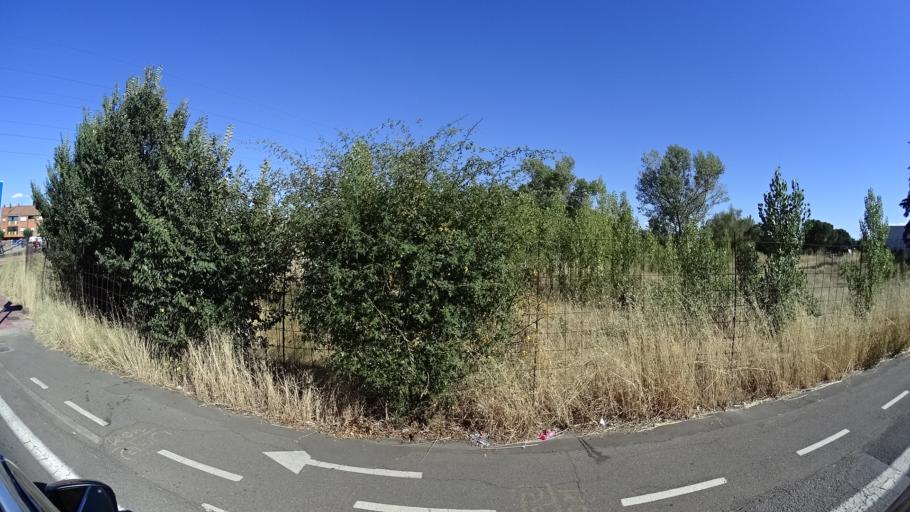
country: ES
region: Castille and Leon
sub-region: Provincia de Leon
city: Leon
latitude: 42.6108
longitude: -5.5543
